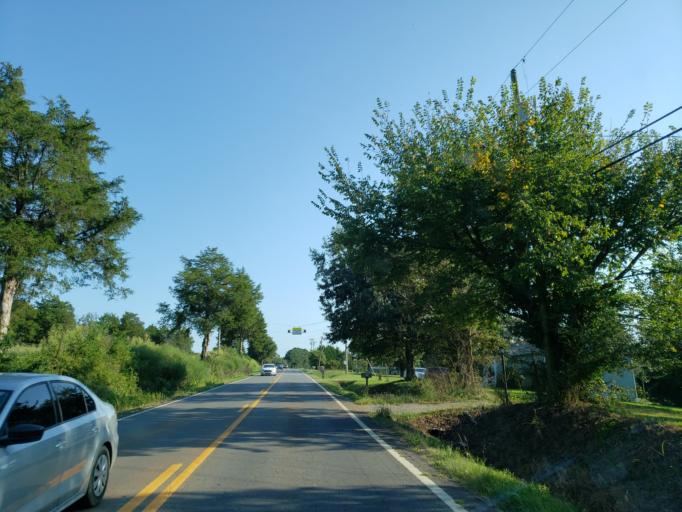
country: US
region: Tennessee
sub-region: Bradley County
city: Wildwood Lake
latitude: 35.0537
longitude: -84.8067
